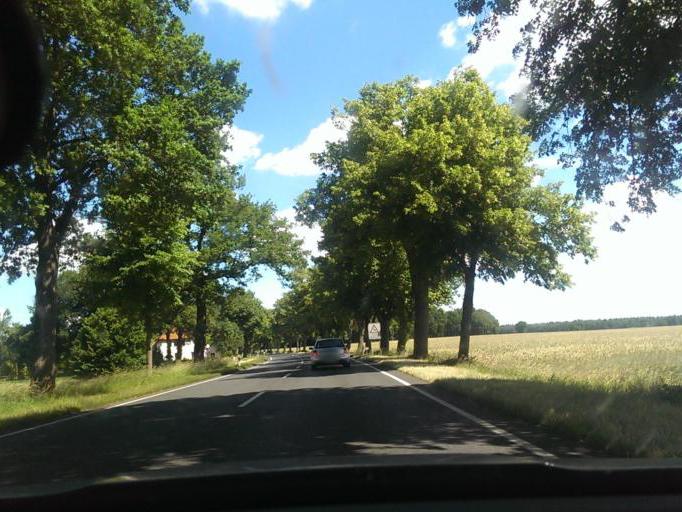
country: DE
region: Lower Saxony
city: Verden
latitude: 52.9817
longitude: 9.2610
